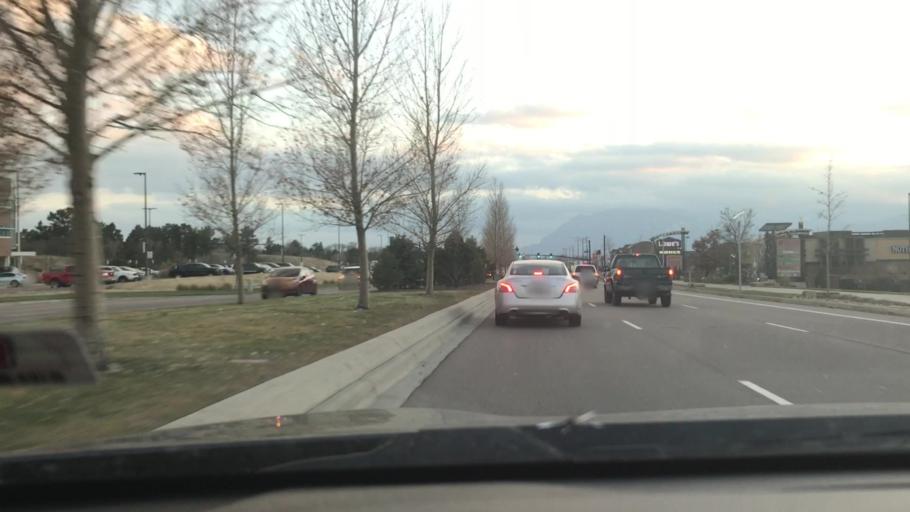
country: US
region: Colorado
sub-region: El Paso County
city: Colorado Springs
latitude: 38.9028
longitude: -104.8175
